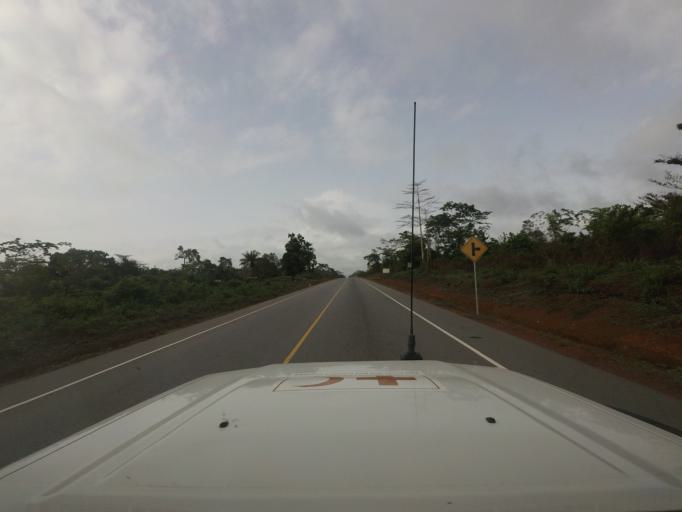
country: LR
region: Bong
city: Gbarnga
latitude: 7.0295
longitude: -9.2708
